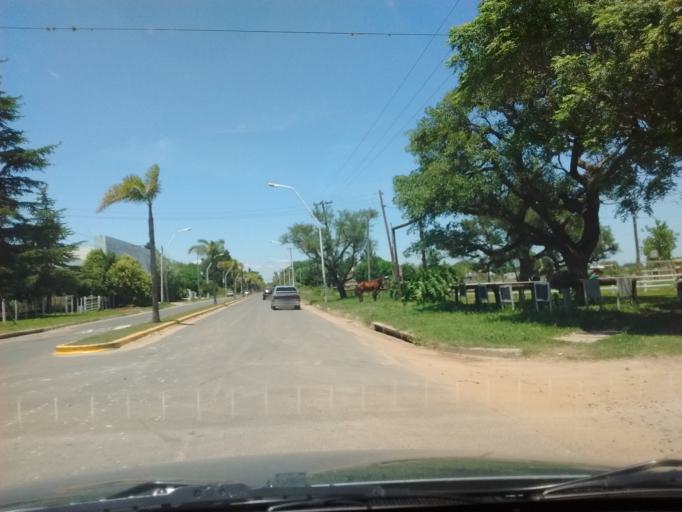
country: AR
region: Entre Rios
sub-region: Departamento de Gualeguay
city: Gualeguay
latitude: -33.1315
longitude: -59.3235
